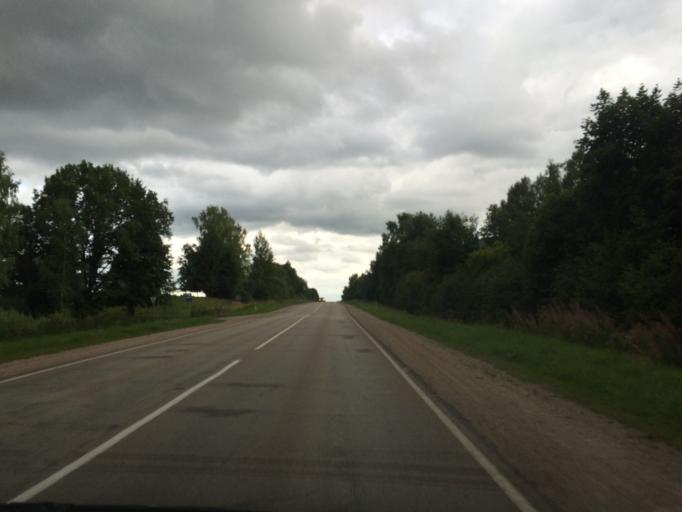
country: LV
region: Rezekne
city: Rezekne
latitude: 56.5634
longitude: 27.3656
